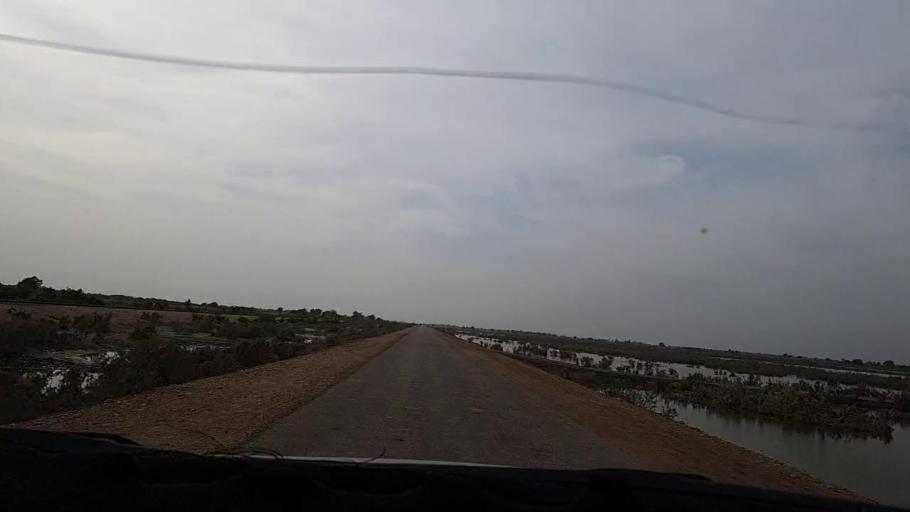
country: PK
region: Sindh
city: Pithoro
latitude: 25.5158
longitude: 69.2896
